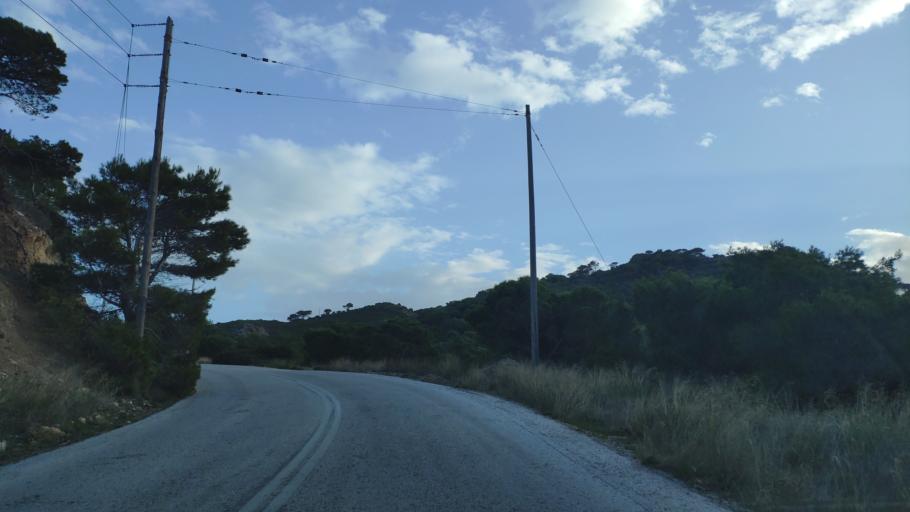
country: GR
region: Attica
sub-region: Nomarchia Anatolikis Attikis
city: Limin Mesoyaias
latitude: 37.9121
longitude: 24.0155
